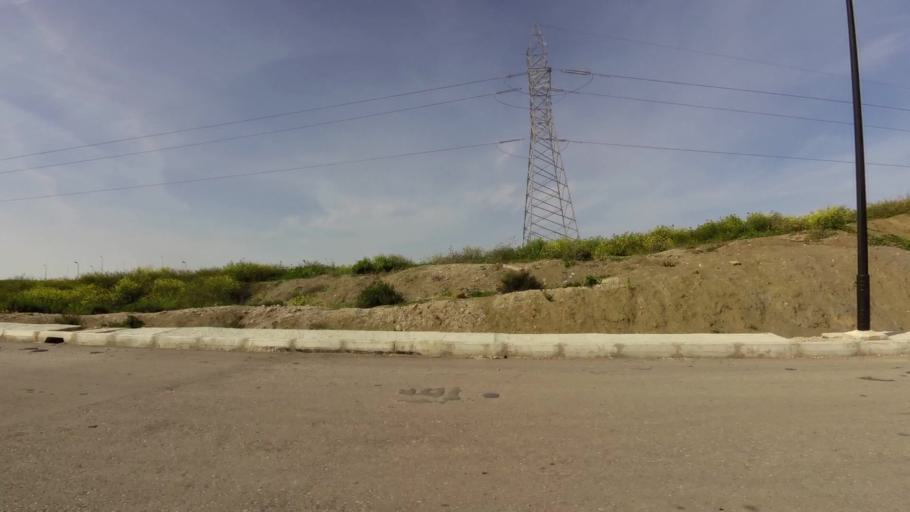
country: MA
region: Tanger-Tetouan
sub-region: Tanger-Assilah
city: Tangier
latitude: 35.7059
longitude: -5.8131
